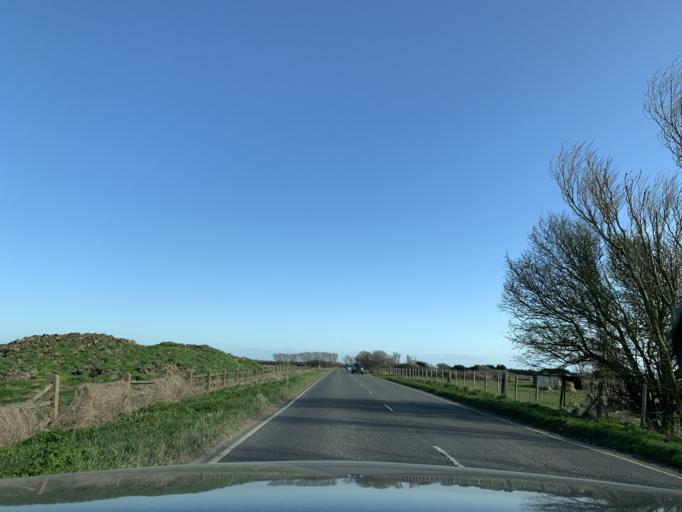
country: GB
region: England
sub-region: Kent
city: Lydd
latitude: 50.9460
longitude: 0.9232
